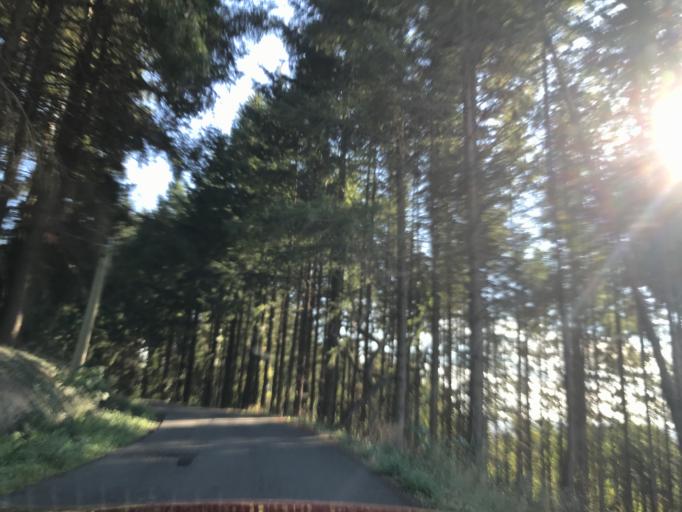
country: FR
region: Auvergne
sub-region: Departement du Puy-de-Dome
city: Escoutoux
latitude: 45.7796
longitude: 3.6066
